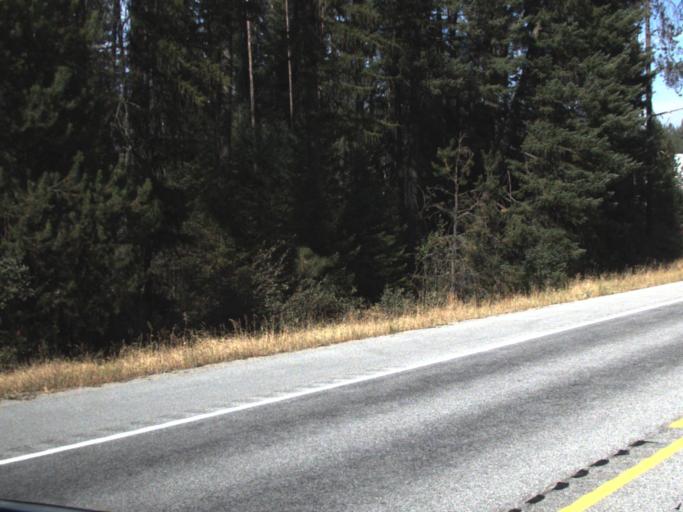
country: US
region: Washington
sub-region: Pend Oreille County
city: Newport
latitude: 48.1545
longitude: -117.1022
